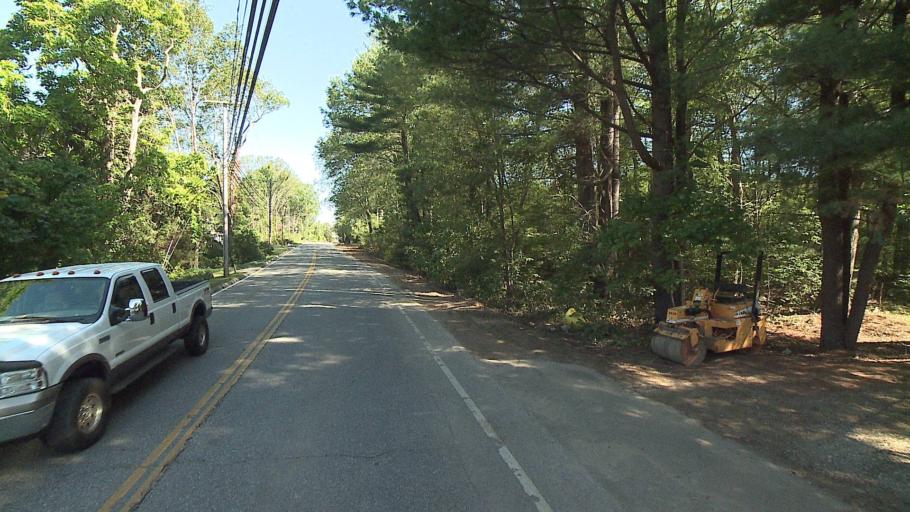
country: US
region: Connecticut
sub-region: Windham County
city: Plainfield Village
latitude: 41.6522
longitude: -71.9307
